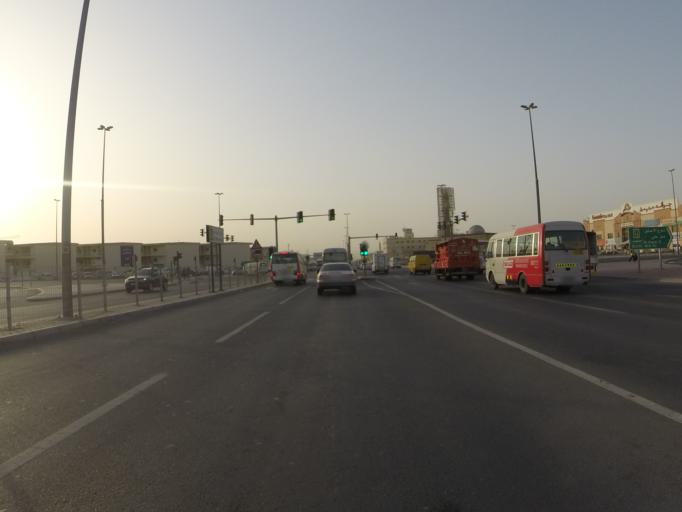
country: AE
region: Dubai
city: Dubai
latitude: 25.1304
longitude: 55.2319
